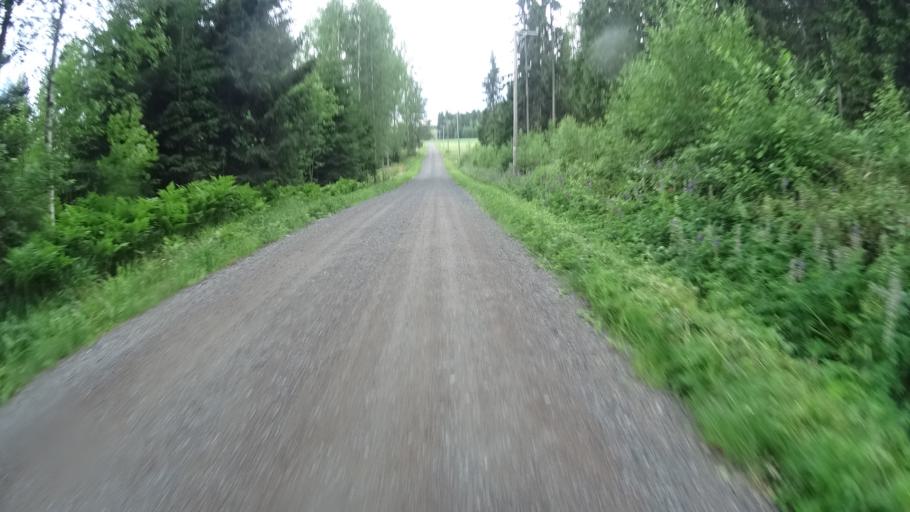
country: FI
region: Uusimaa
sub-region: Helsinki
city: Karkkila
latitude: 60.5876
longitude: 24.1639
